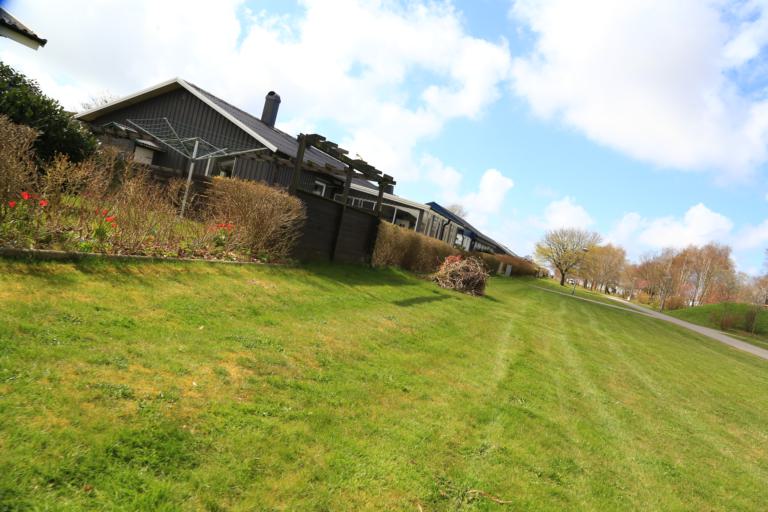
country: SE
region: Halland
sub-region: Varbergs Kommun
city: Varberg
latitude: 57.1081
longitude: 12.2801
